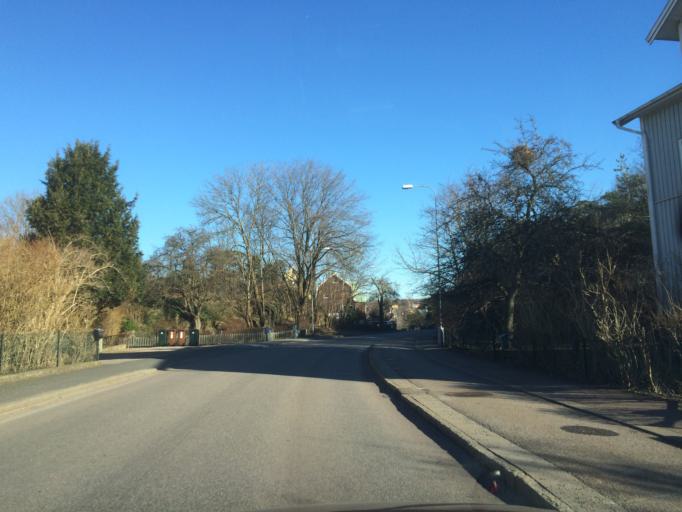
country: SE
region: Vaestra Goetaland
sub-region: Goteborg
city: Majorna
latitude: 57.6738
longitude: 11.8966
